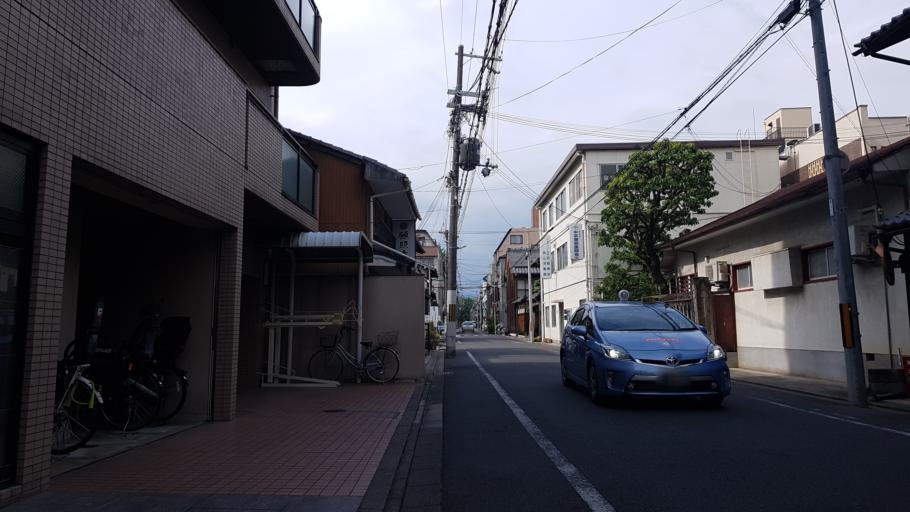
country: JP
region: Kyoto
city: Kyoto
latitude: 35.0129
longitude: 135.7650
